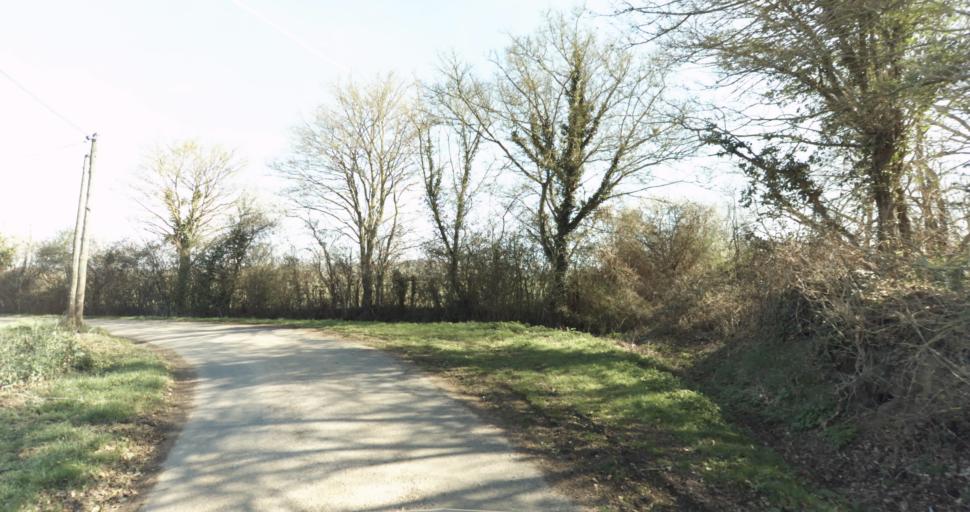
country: FR
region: Lower Normandy
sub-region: Departement du Calvados
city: Saint-Pierre-sur-Dives
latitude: 49.0319
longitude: 0.0110
